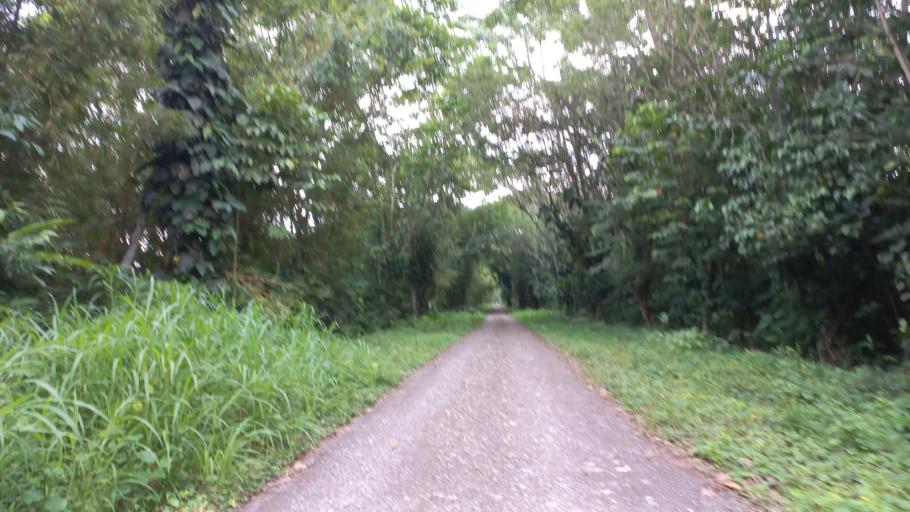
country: CO
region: Antioquia
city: Carepa
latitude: 7.7725
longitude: -76.6666
